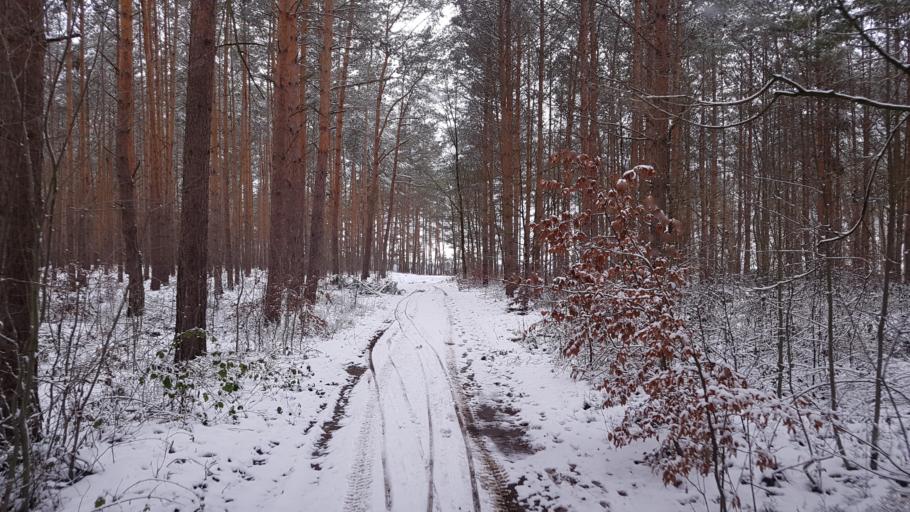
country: DE
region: Brandenburg
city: Crinitz
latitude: 51.7299
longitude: 13.7709
